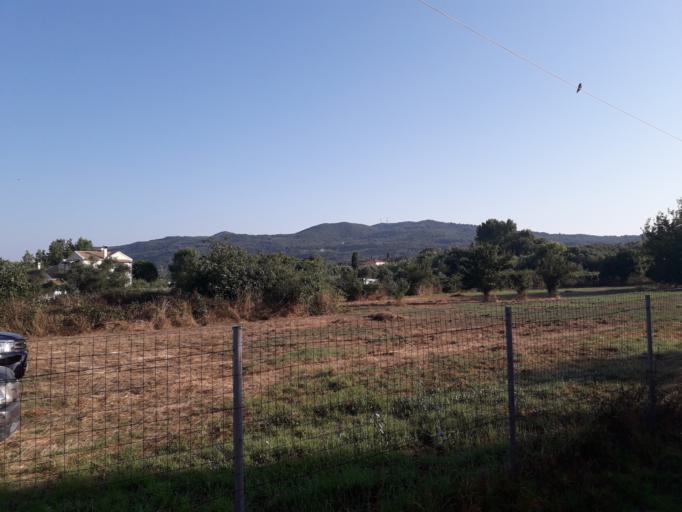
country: GR
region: Ionian Islands
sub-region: Nomos Kerkyras
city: Perivoli
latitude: 39.4301
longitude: 19.9533
